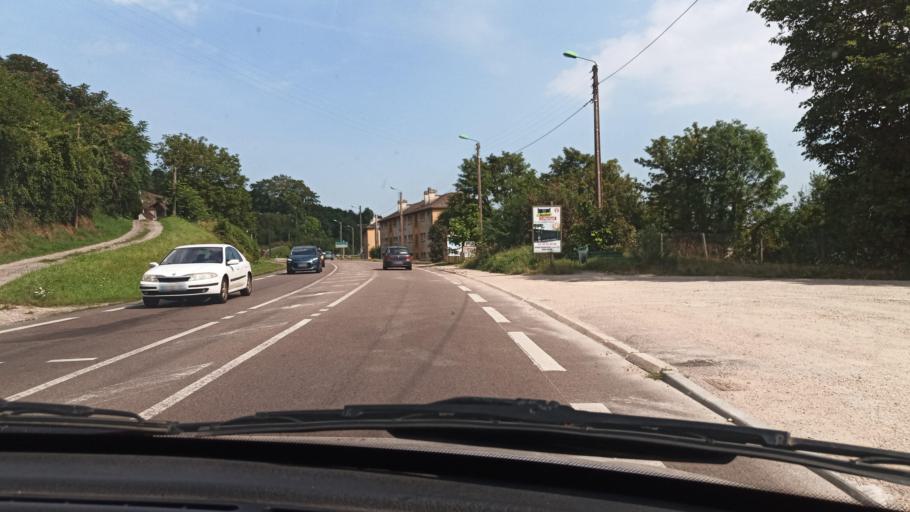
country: FR
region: Bourgogne
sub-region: Departement de l'Yonne
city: Saint-Martin-du-Tertre
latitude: 48.2018
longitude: 3.2646
